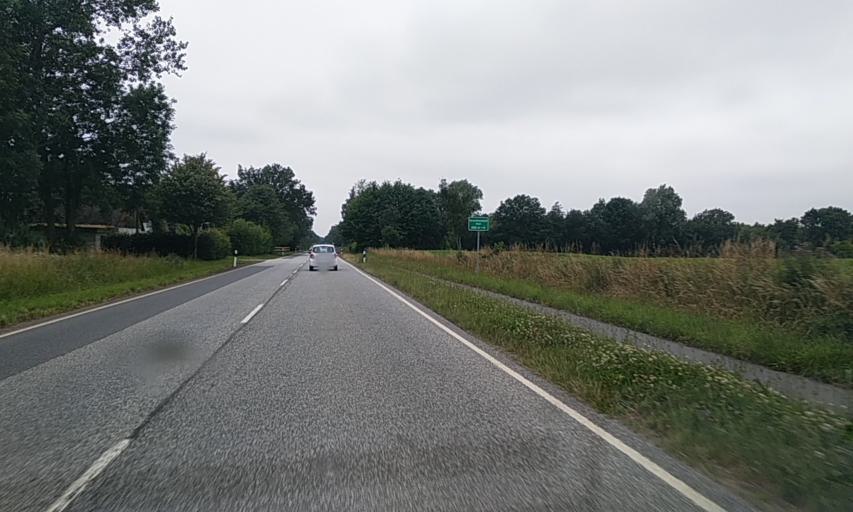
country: DE
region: Schleswig-Holstein
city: Loit
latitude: 54.6255
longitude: 9.7133
